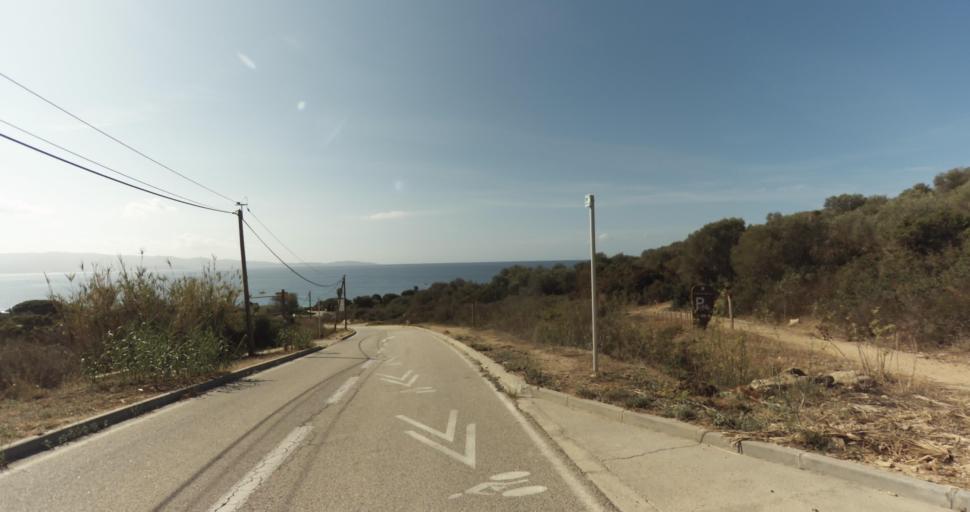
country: FR
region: Corsica
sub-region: Departement de la Corse-du-Sud
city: Ajaccio
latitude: 41.9131
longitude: 8.6437
